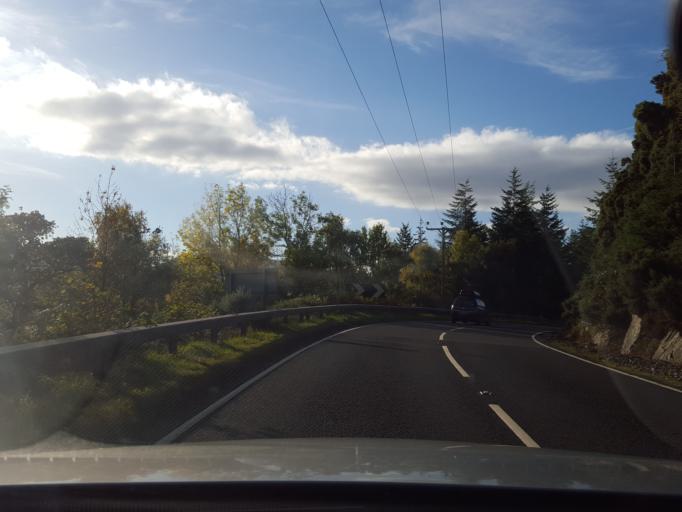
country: GB
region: Scotland
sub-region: Highland
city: Beauly
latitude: 57.2185
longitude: -4.5834
